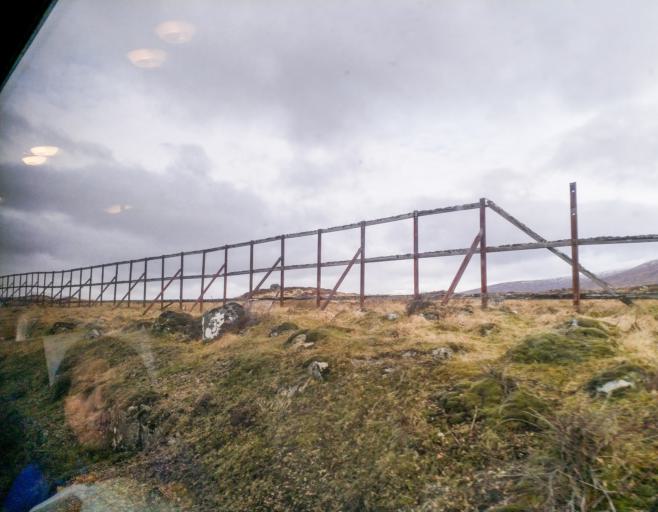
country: GB
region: Scotland
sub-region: Highland
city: Spean Bridge
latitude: 56.7020
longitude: -4.5805
